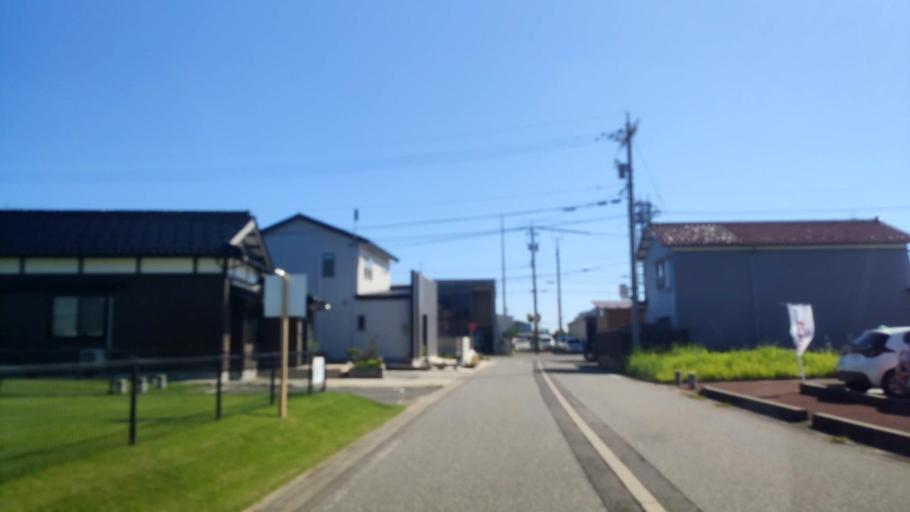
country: JP
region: Ishikawa
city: Nanao
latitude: 37.4415
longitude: 137.2707
